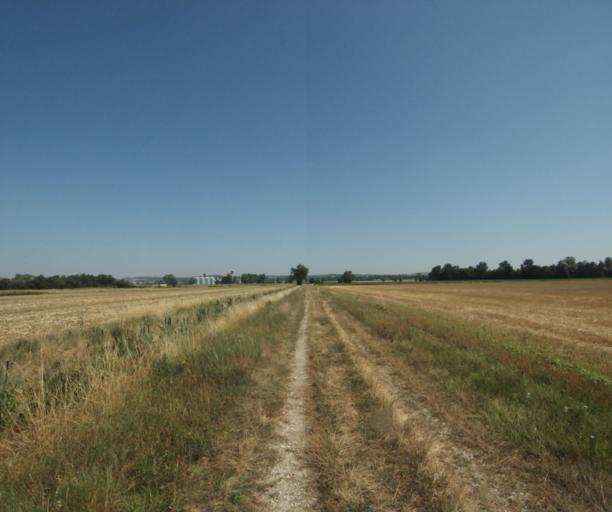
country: FR
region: Midi-Pyrenees
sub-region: Departement de la Haute-Garonne
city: Revel
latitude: 43.5143
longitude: 1.9640
